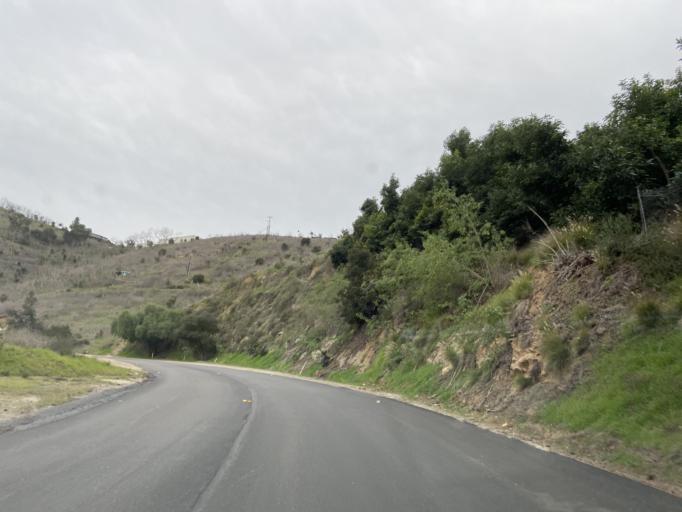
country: US
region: California
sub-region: San Diego County
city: Valley Center
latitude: 33.3067
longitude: -117.0197
